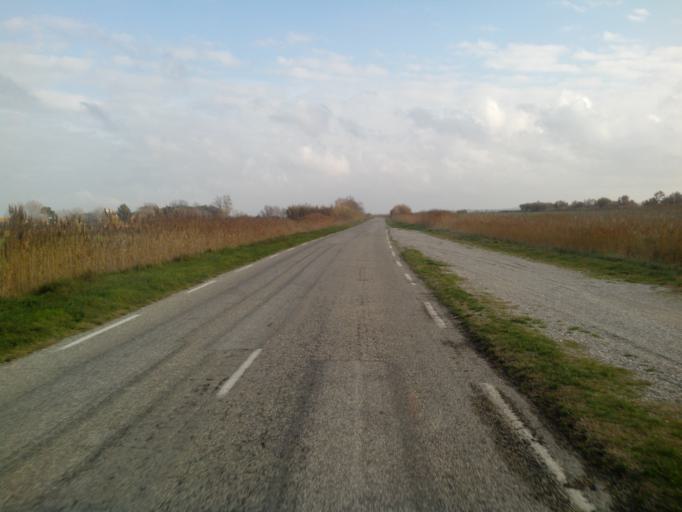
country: FR
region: Provence-Alpes-Cote d'Azur
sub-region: Departement des Bouches-du-Rhone
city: Arles
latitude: 43.5669
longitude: 4.5717
